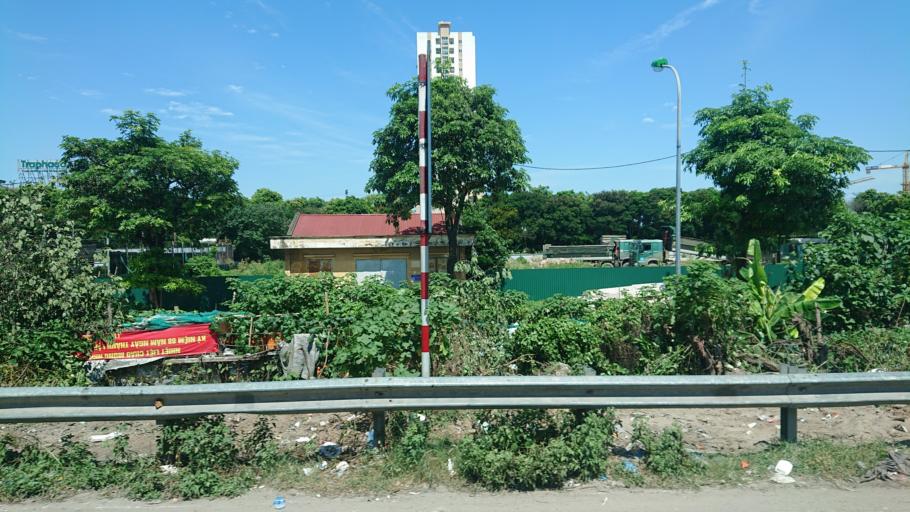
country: VN
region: Ha Noi
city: Van Dien
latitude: 20.9625
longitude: 105.8471
